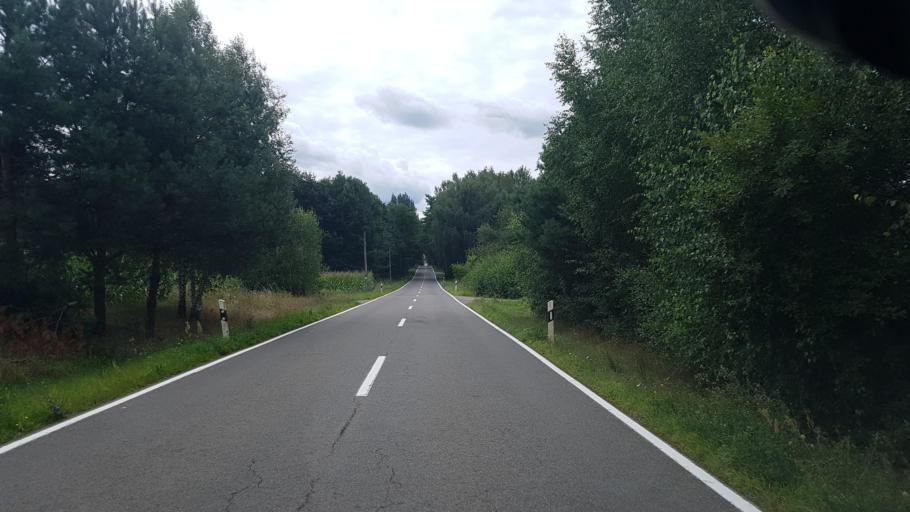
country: DE
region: Brandenburg
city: Spremberg
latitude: 51.6059
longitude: 14.3419
